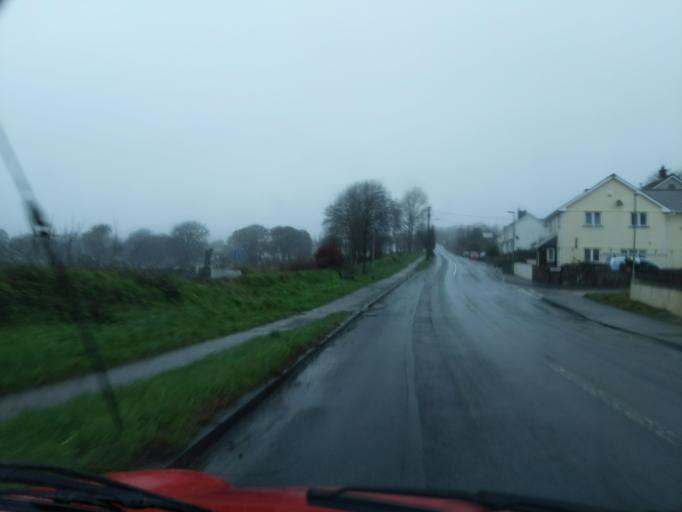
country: GB
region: England
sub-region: Cornwall
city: Callington
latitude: 50.5090
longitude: -4.3136
